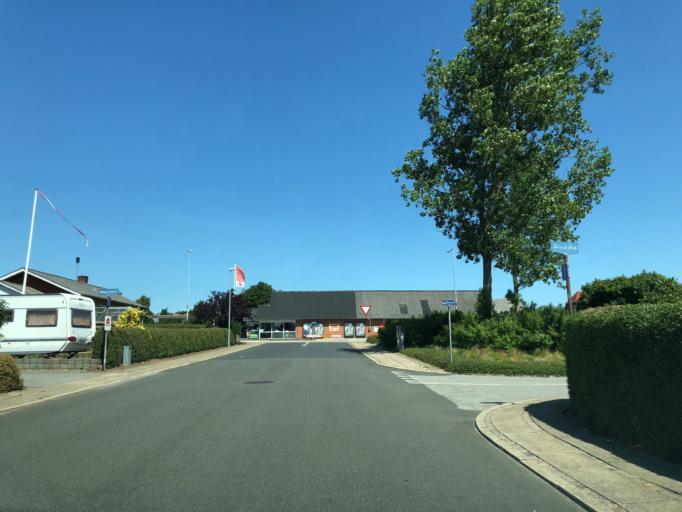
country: DK
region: Central Jutland
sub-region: Holstebro Kommune
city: Holstebro
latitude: 56.3637
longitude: 8.6907
